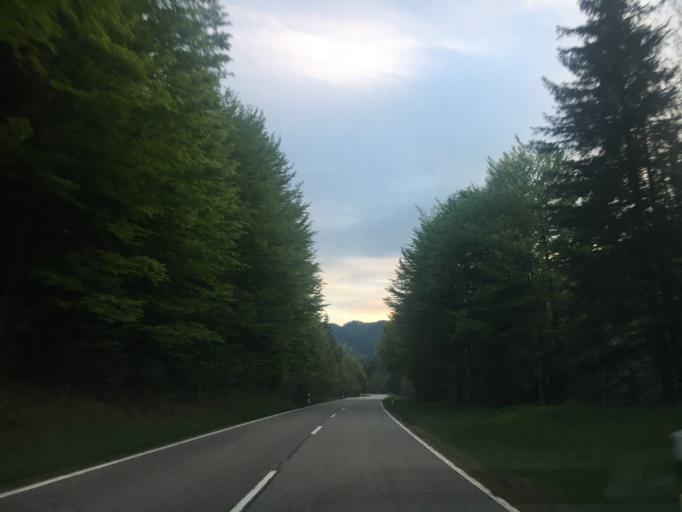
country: DE
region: Bavaria
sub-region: Upper Bavaria
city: Lenggries
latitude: 47.5979
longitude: 11.5646
